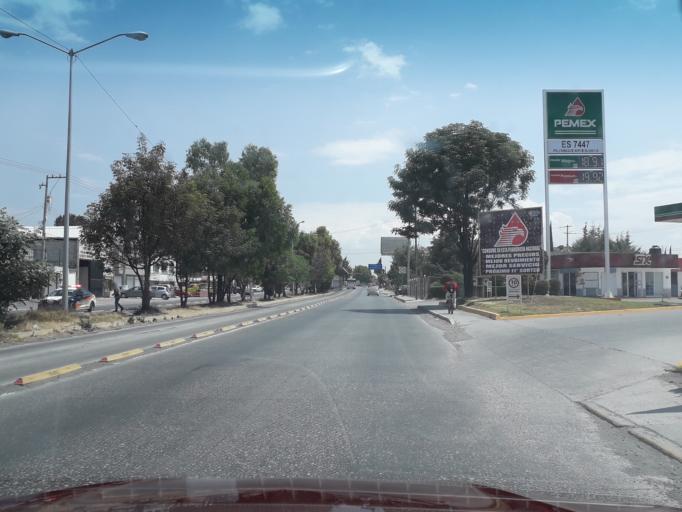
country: MX
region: Puebla
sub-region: Puebla
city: El Capulo (La Quebradora)
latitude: 18.9720
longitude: -98.2626
